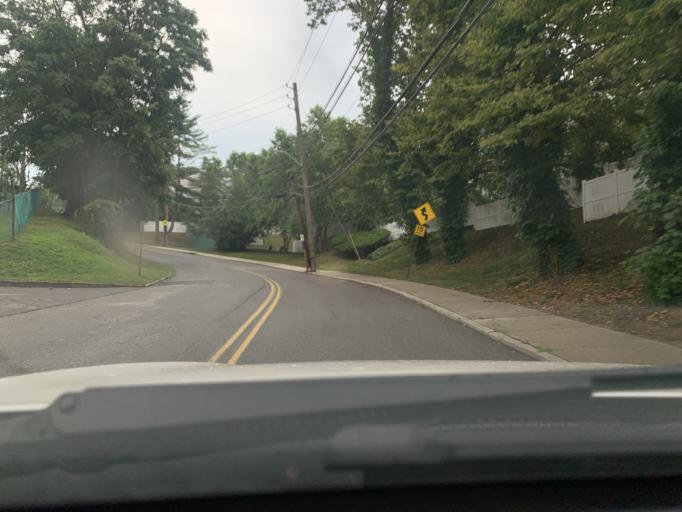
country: US
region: New York
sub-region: Westchester County
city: Ossining
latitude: 41.1687
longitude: -73.8622
